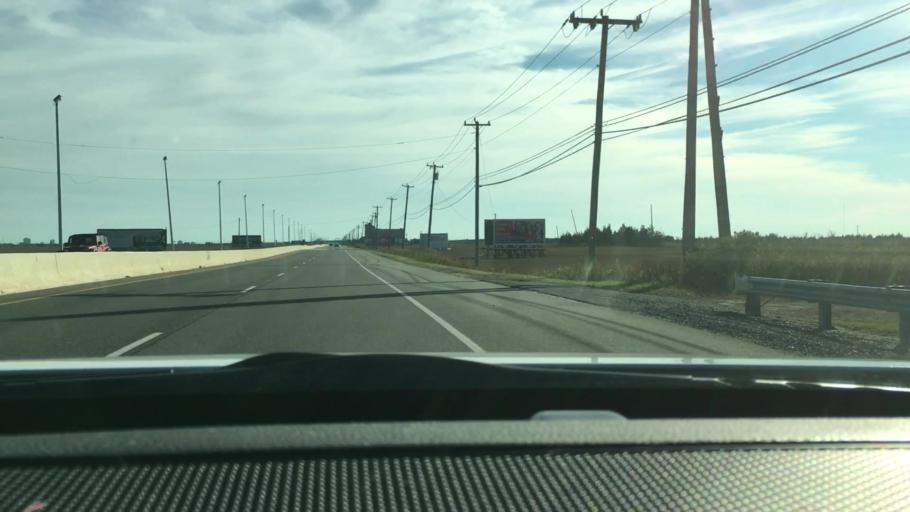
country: US
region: New Jersey
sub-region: Atlantic County
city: Absecon
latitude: 39.4145
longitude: -74.4915
